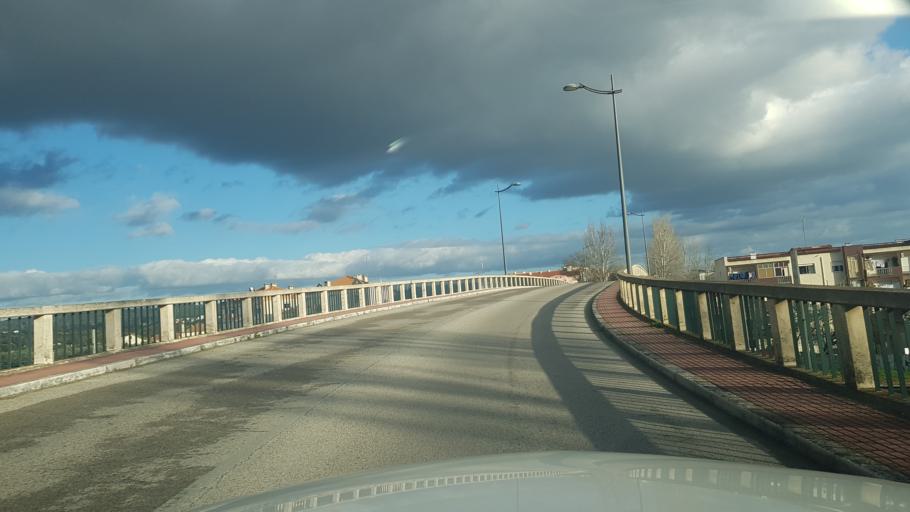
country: PT
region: Santarem
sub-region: Entroncamento
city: Entroncamento
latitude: 39.4663
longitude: -8.4703
